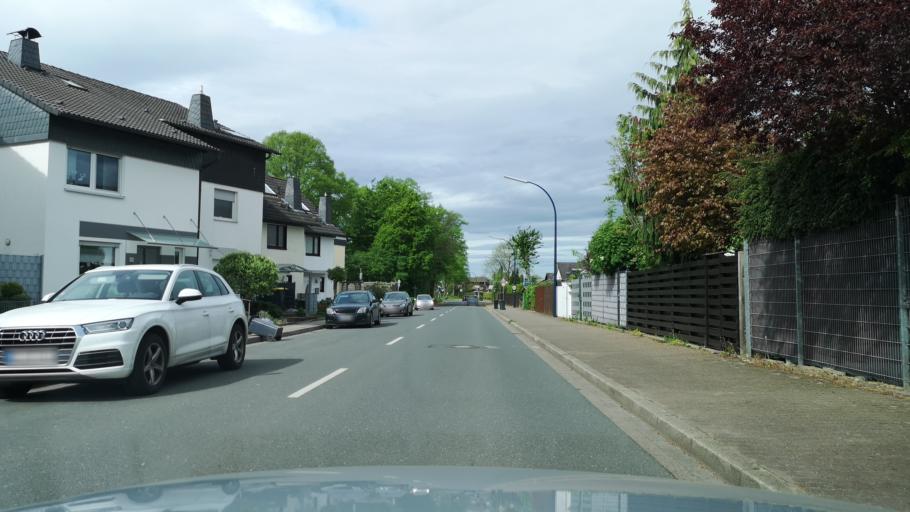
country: DE
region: North Rhine-Westphalia
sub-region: Regierungsbezirk Arnsberg
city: Holzwickede
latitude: 51.4979
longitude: 7.6285
